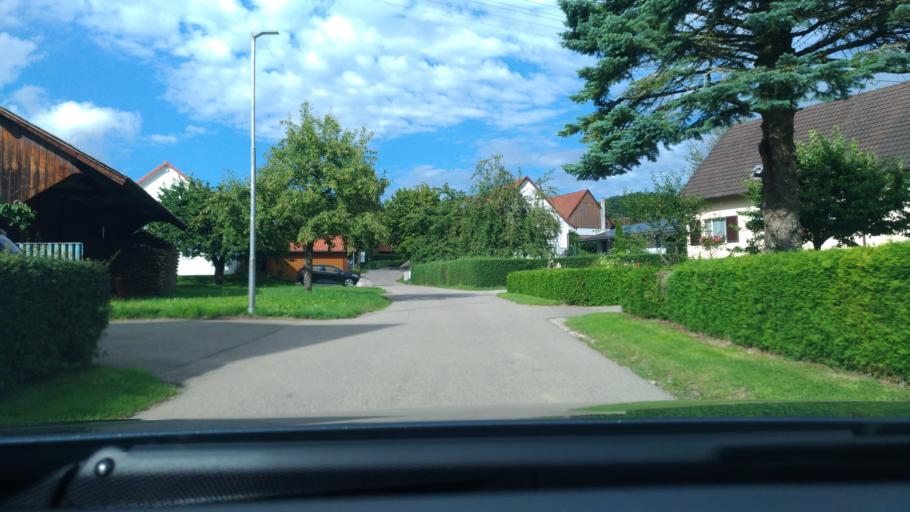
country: DE
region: Baden-Wuerttemberg
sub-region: Tuebingen Region
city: Sipplingen
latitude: 47.8162
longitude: 9.1134
